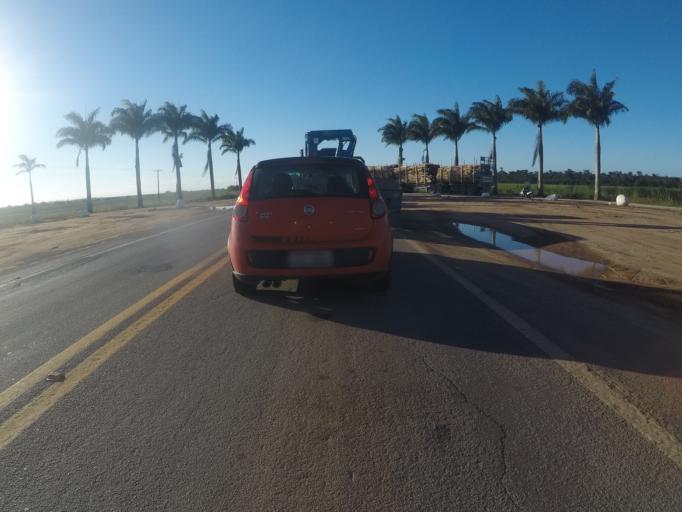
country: BR
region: Espirito Santo
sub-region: Conceicao Da Barra
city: Conceicao da Barra
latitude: -18.4596
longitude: -39.9300
